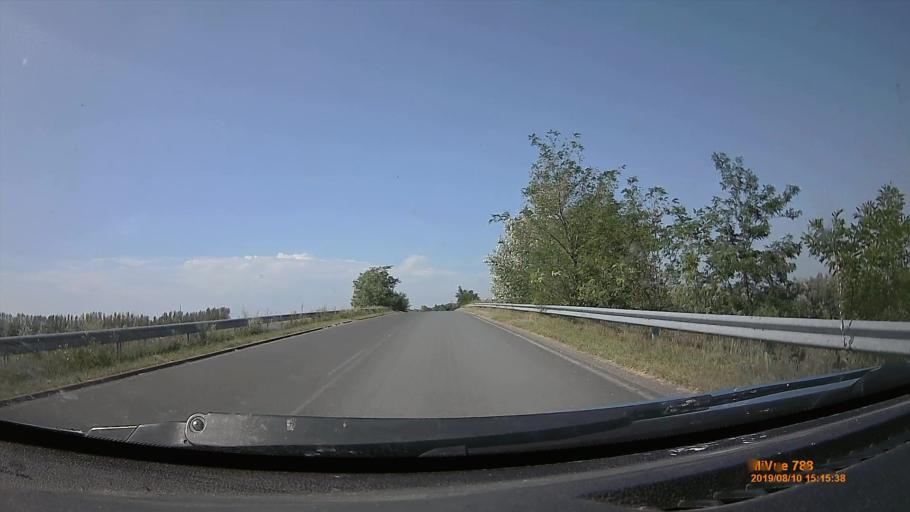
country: HU
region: Somogy
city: Fonyod
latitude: 46.7005
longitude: 17.5568
